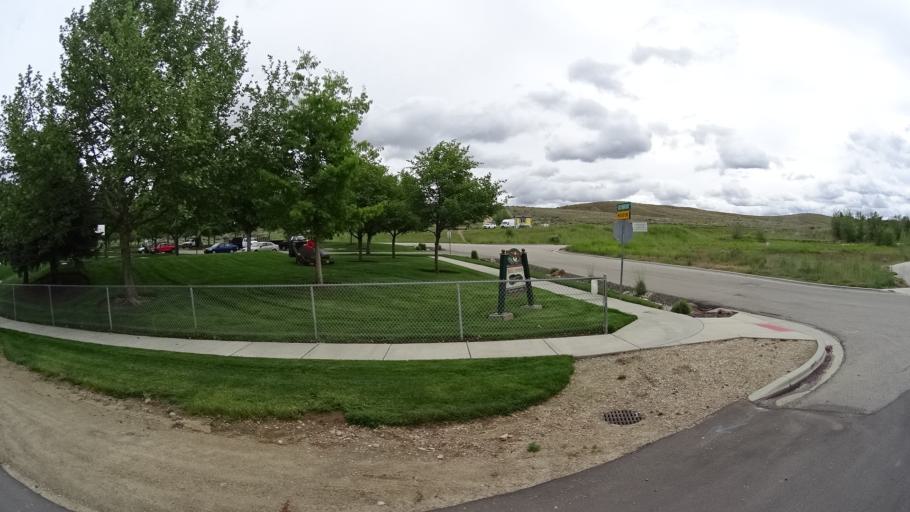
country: US
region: Idaho
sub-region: Ada County
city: Eagle
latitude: 43.7116
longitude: -116.3156
